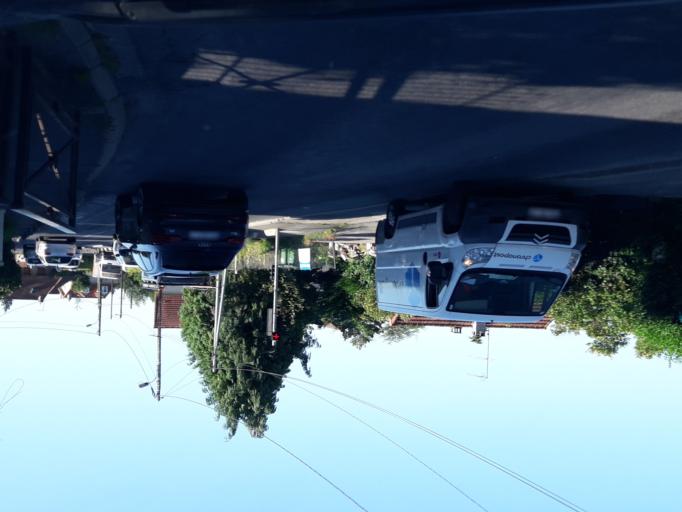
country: FR
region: Ile-de-France
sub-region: Departement de l'Essonne
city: Itteville
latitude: 48.5215
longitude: 2.3494
